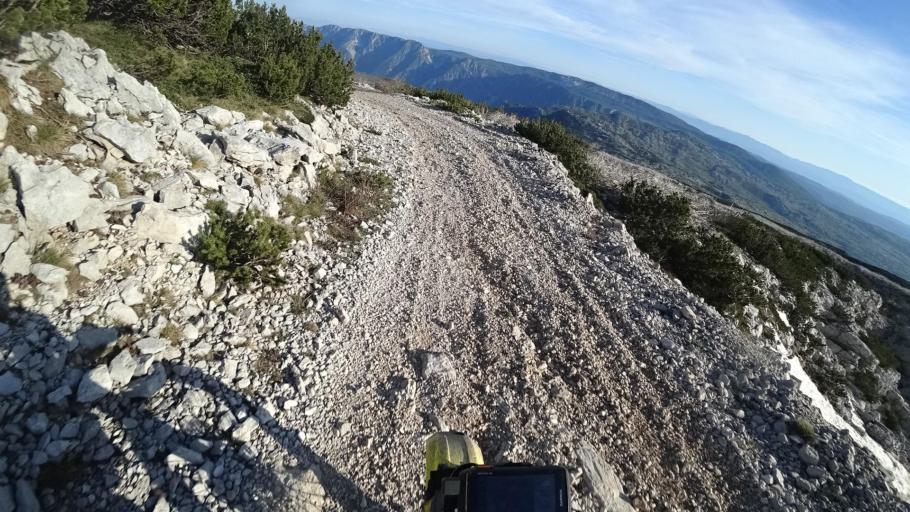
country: BA
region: Federation of Bosnia and Herzegovina
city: Kocerin
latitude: 43.5927
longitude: 17.5396
